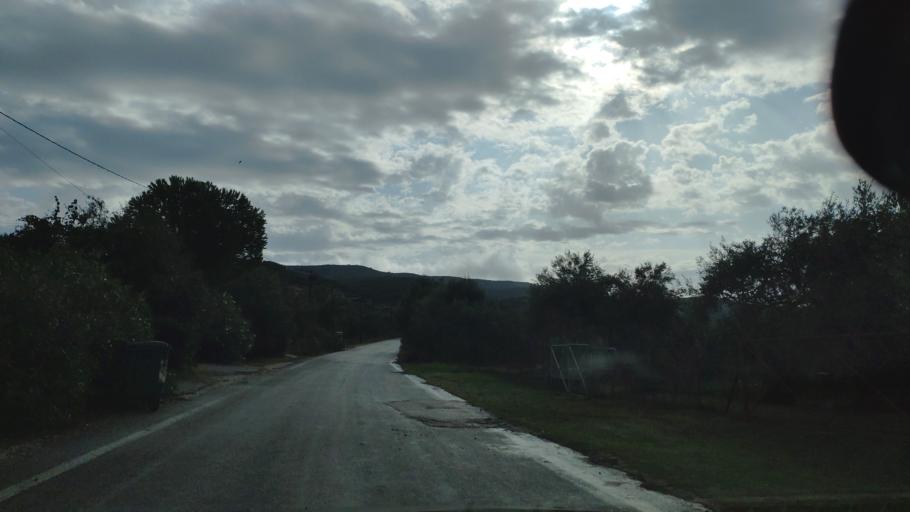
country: GR
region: West Greece
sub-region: Nomos Aitolias kai Akarnanias
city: Sardinia
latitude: 38.8905
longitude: 21.2234
